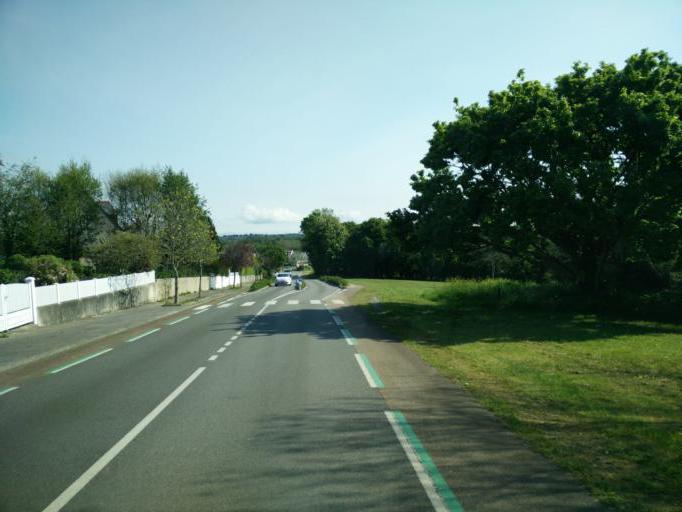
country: FR
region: Brittany
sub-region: Departement du Finistere
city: Crozon
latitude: 48.2456
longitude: -4.4743
